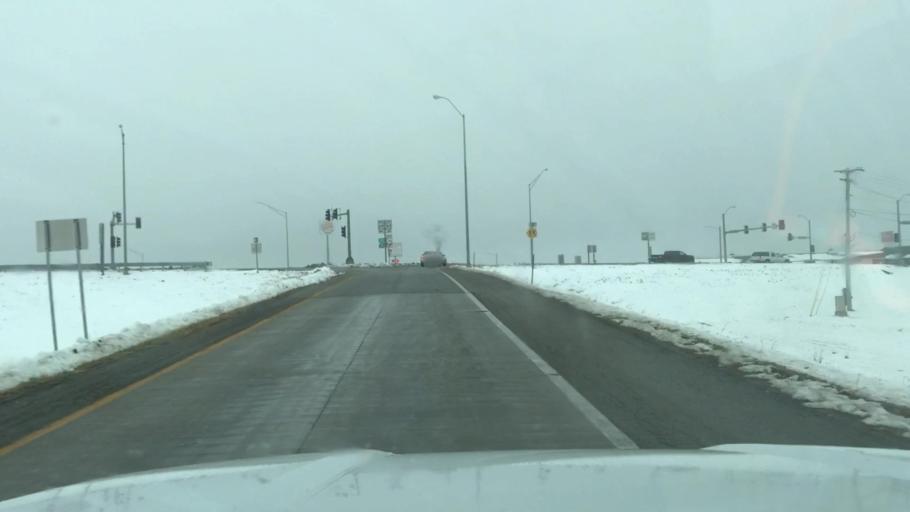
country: US
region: Missouri
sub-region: Clinton County
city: Cameron
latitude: 39.7539
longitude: -94.2354
